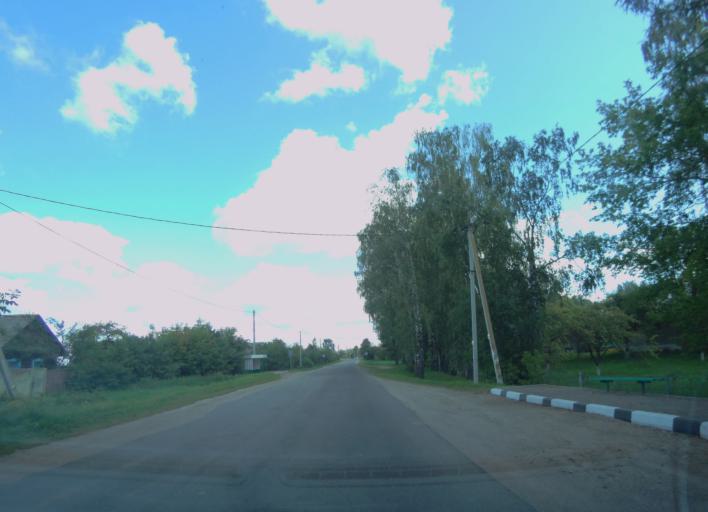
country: BY
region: Minsk
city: Zyembin
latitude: 54.3774
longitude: 28.3835
